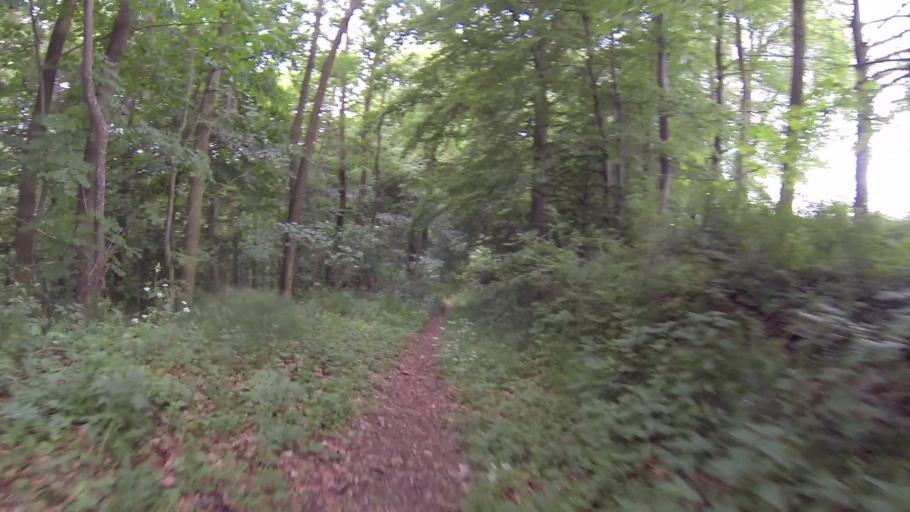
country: DE
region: Baden-Wuerttemberg
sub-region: Tuebingen Region
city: Blaubeuren
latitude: 48.4190
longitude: 9.7886
